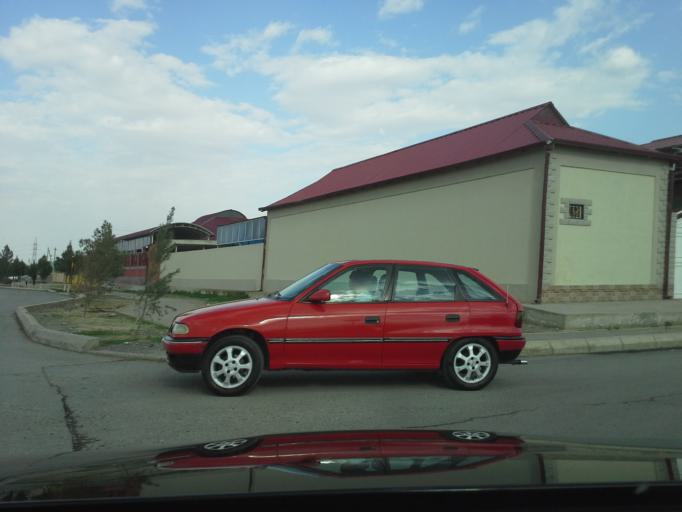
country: TM
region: Ahal
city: Ashgabat
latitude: 37.9929
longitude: 58.2917
